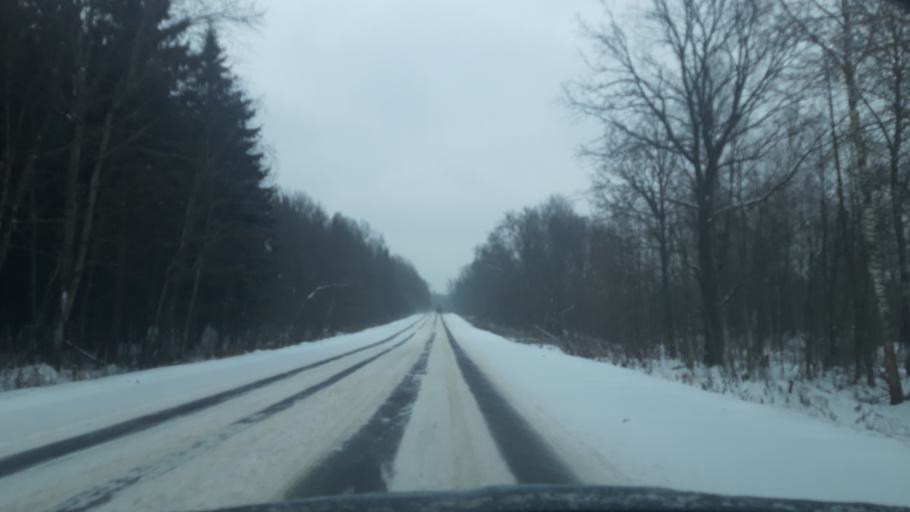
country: RU
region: Moskovskaya
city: Avtopoligon
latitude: 56.2767
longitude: 37.3694
